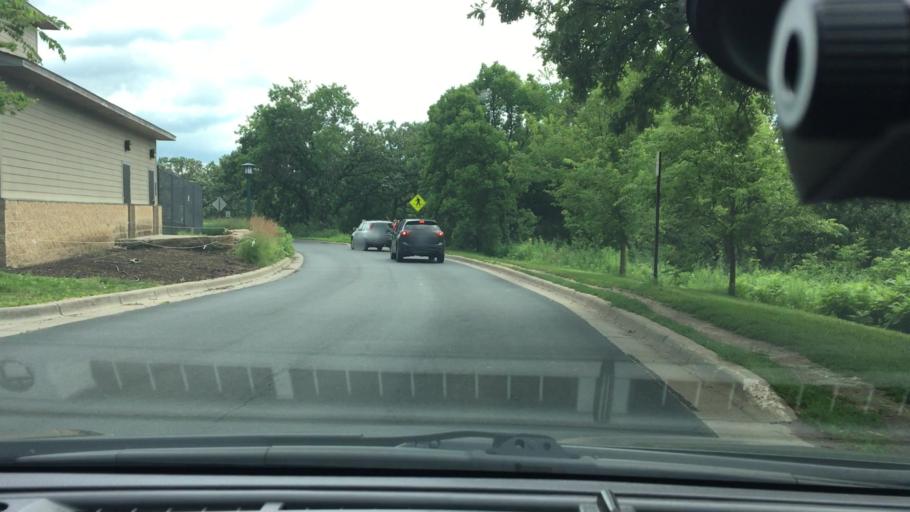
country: US
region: Minnesota
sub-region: Dakota County
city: Mendota Heights
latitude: 44.9167
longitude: -93.2066
